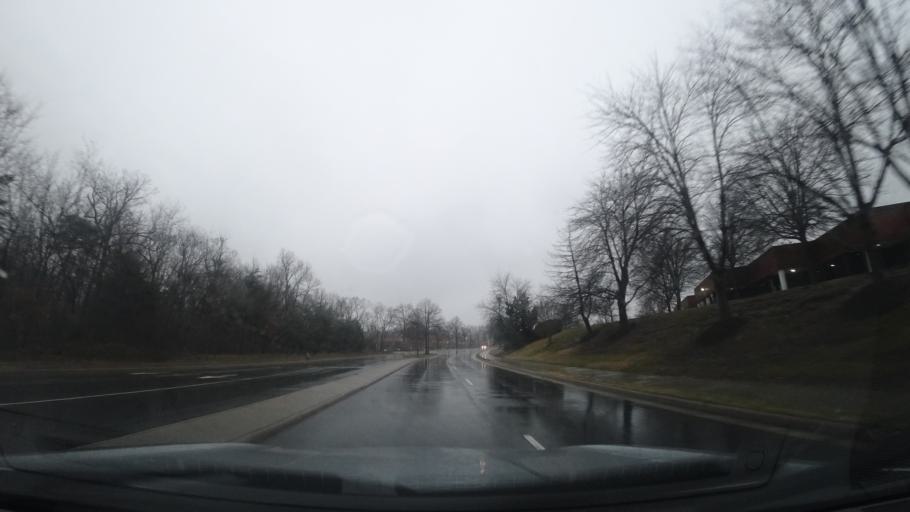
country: US
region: Virginia
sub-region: Fairfax County
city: Herndon
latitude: 38.9647
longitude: -77.3720
